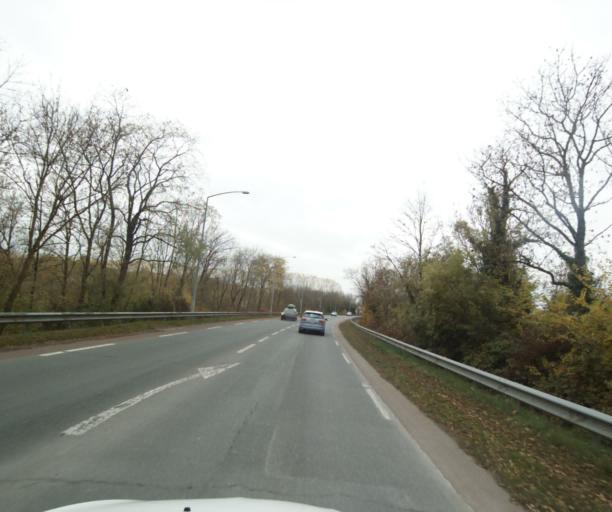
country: FR
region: Poitou-Charentes
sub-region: Departement de la Charente-Maritime
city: Saintes
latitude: 45.7409
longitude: -0.6334
